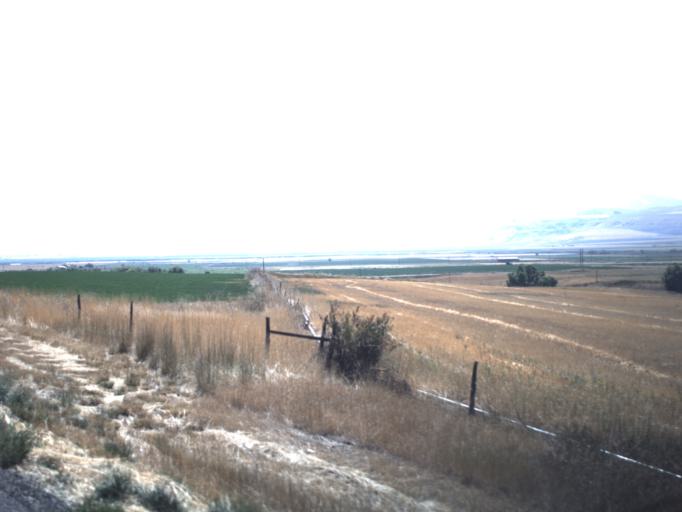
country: US
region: Utah
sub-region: Cache County
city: Benson
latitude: 41.8577
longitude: -111.9759
